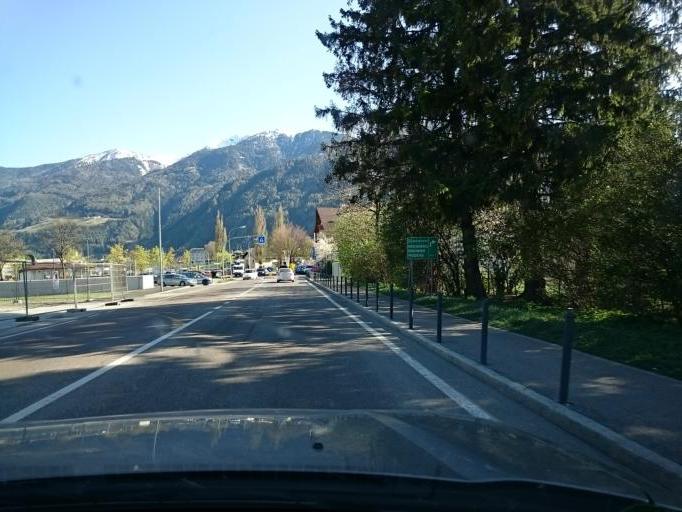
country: IT
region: Trentino-Alto Adige
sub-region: Bolzano
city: Vipiteno
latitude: 46.8939
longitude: 11.4357
